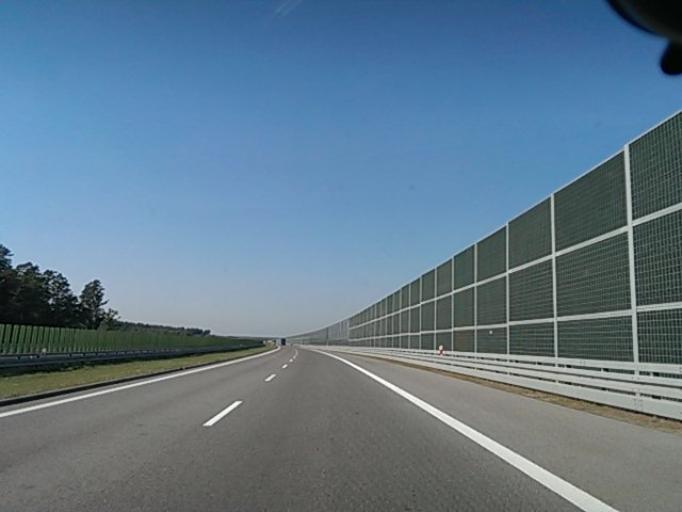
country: PL
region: Subcarpathian Voivodeship
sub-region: Powiat rzeszowski
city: Trzciana
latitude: 50.1184
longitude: 21.7926
